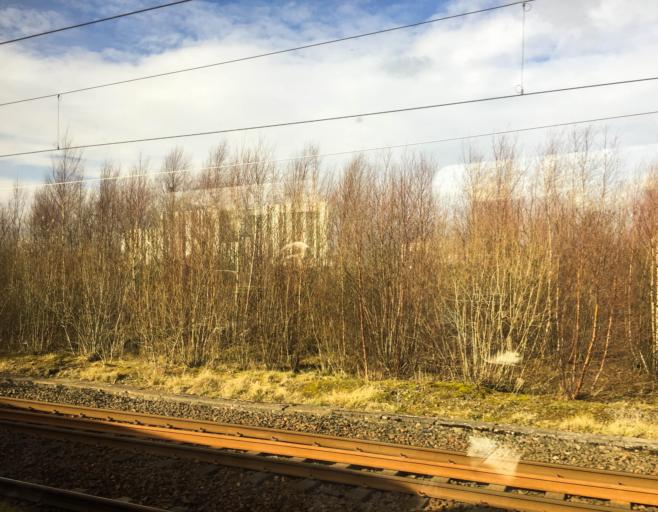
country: GB
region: Scotland
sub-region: North Lanarkshire
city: Glenboig
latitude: 55.8844
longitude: -4.0711
